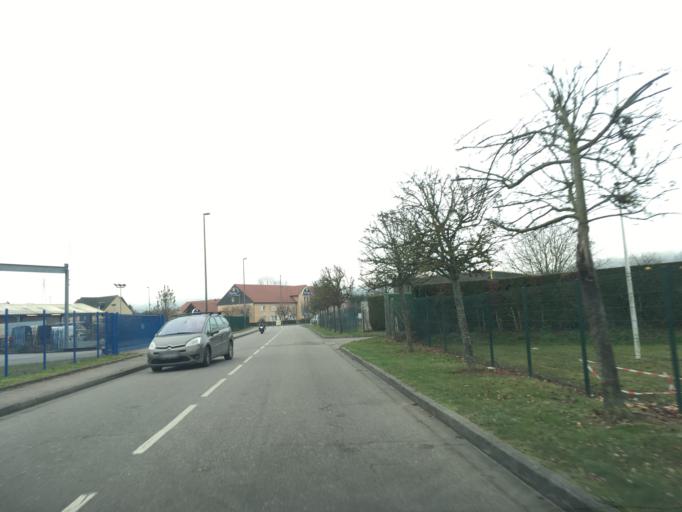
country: FR
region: Haute-Normandie
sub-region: Departement de l'Eure
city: Saint-Marcel
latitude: 49.1061
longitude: 1.4511
